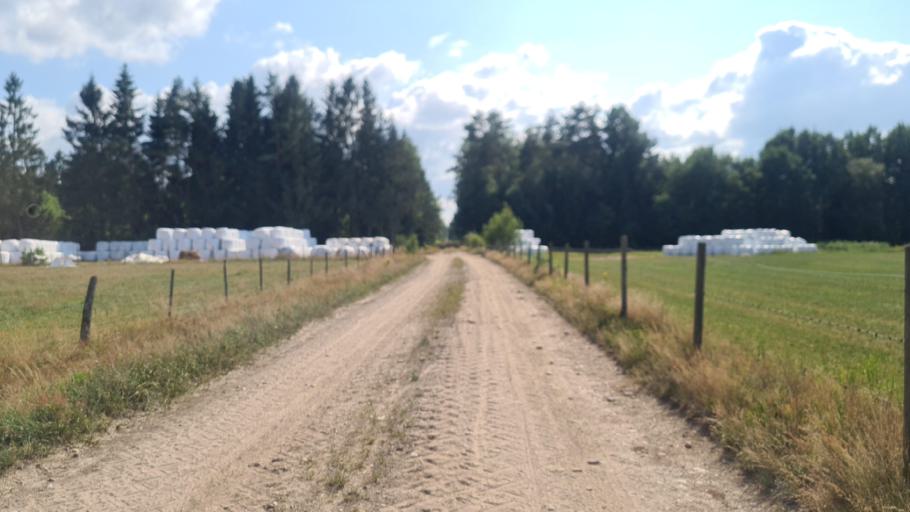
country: SE
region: Kronoberg
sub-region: Ljungby Kommun
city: Ljungby
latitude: 56.7708
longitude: 13.8975
